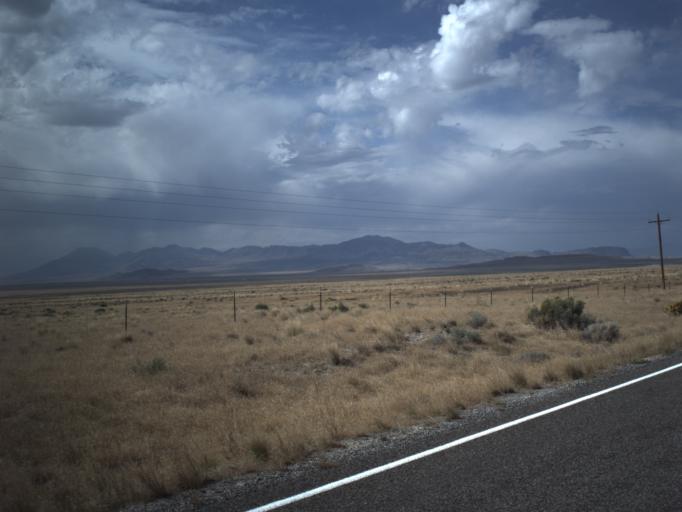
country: US
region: Utah
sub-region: Tooele County
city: Wendover
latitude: 41.4337
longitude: -113.7735
